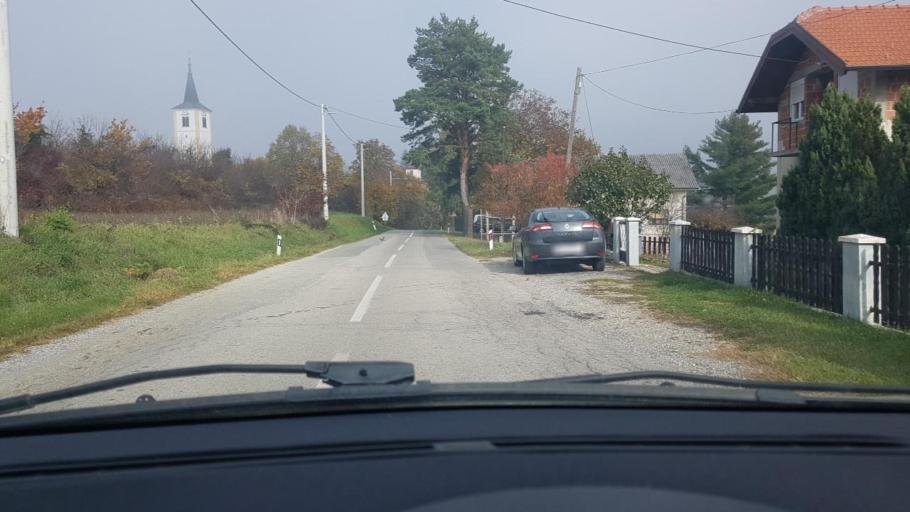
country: HR
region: Krapinsko-Zagorska
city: Zlatar
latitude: 46.1298
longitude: 16.1197
